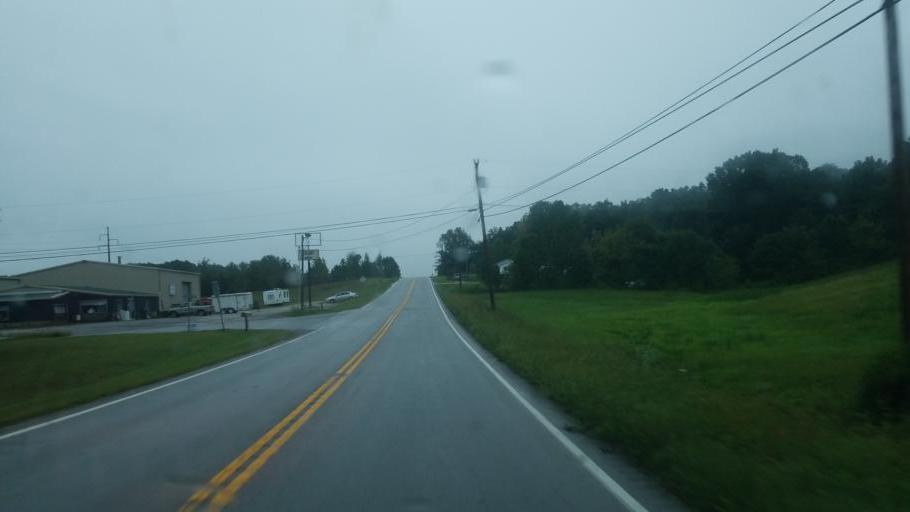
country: US
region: Kentucky
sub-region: Fleming County
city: Flemingsburg
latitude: 38.3832
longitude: -83.6507
